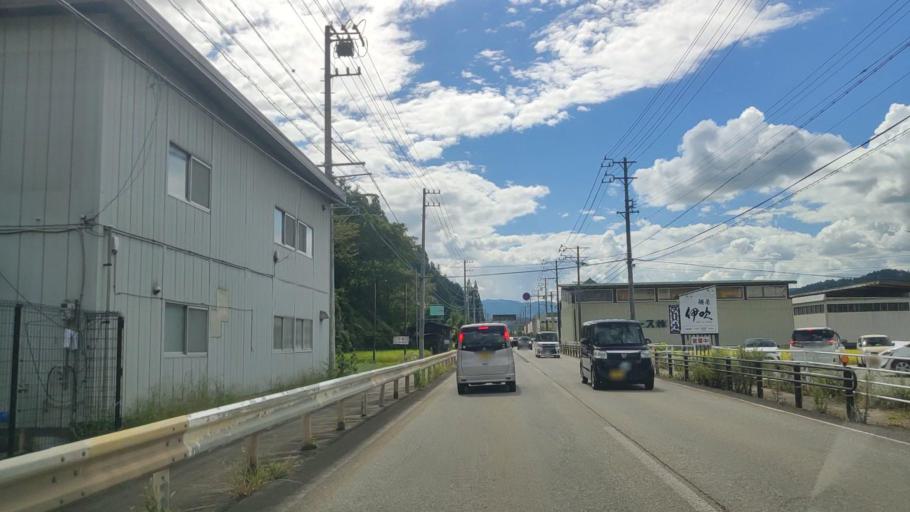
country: JP
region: Gifu
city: Takayama
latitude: 36.1843
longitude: 137.2530
